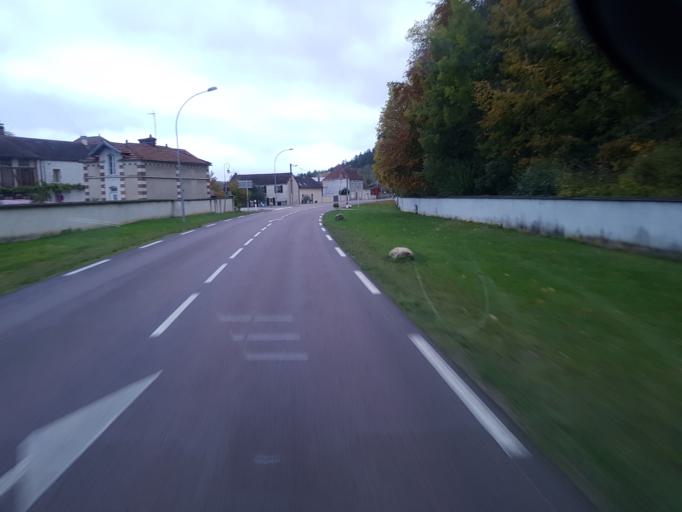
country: FR
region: Champagne-Ardenne
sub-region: Departement de l'Aube
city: Mussy-sur-Seine
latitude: 47.9811
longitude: 4.4982
